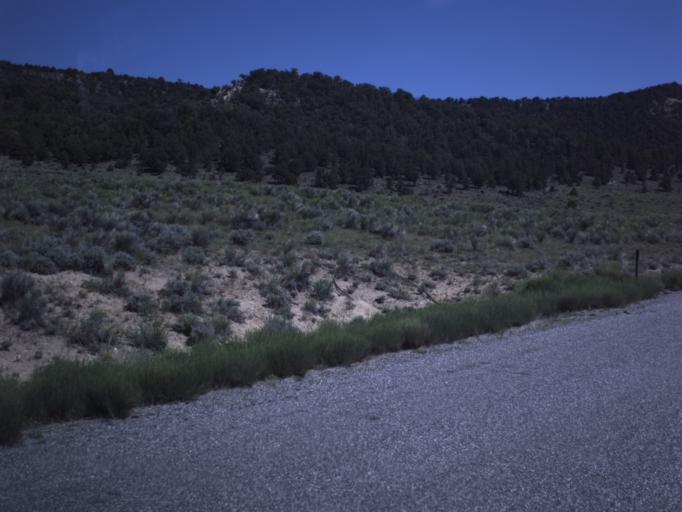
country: US
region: Utah
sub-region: Wayne County
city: Loa
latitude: 38.6296
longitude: -111.4453
